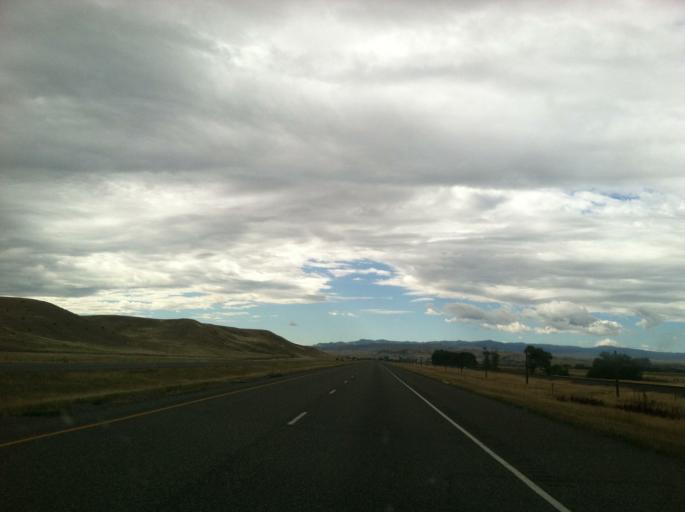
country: US
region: Montana
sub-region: Park County
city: Livingston
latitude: 45.7132
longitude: -110.4226
